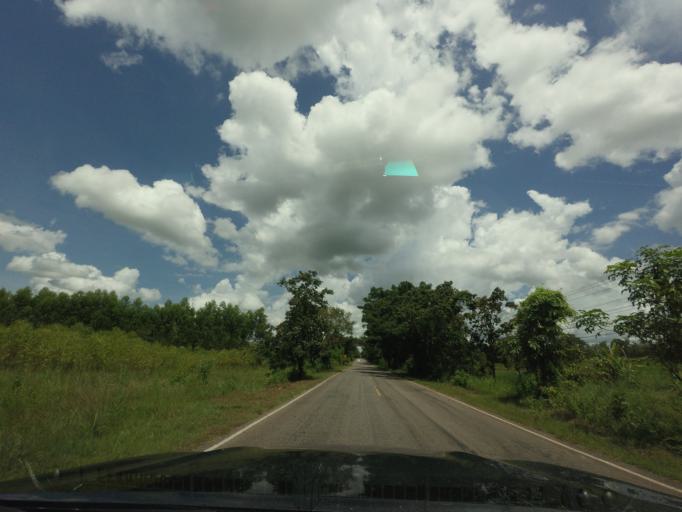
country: TH
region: Changwat Udon Thani
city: Phibun Rak
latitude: 17.5971
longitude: 103.0610
